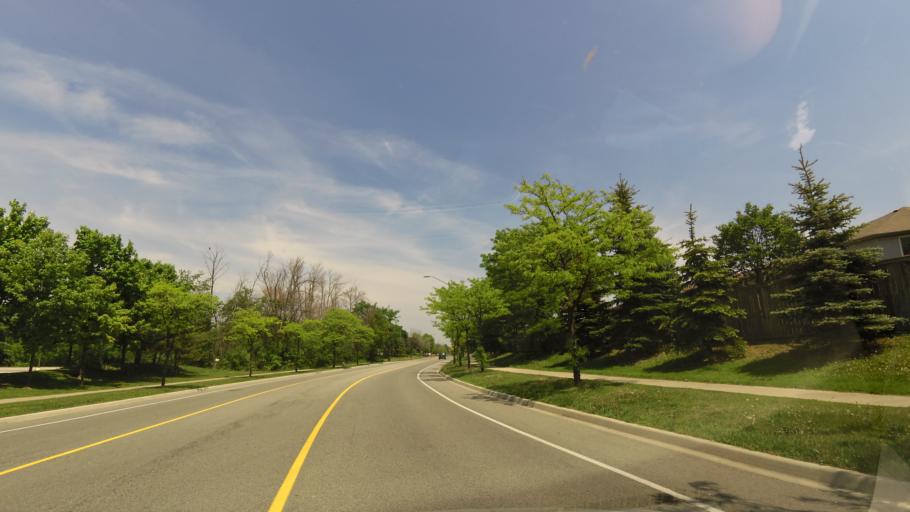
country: CA
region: Ontario
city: Mississauga
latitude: 43.5349
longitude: -79.7141
